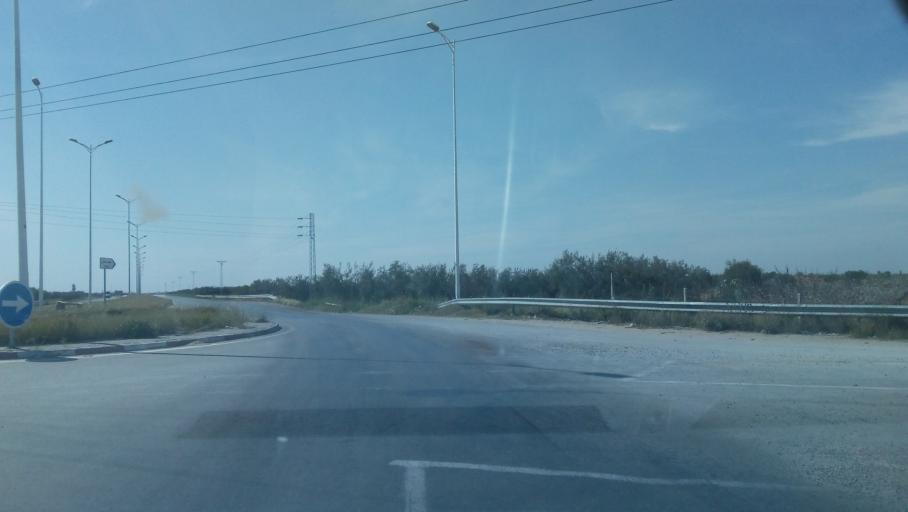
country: TN
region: Safaqis
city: Al Qarmadah
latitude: 34.8630
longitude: 10.8049
